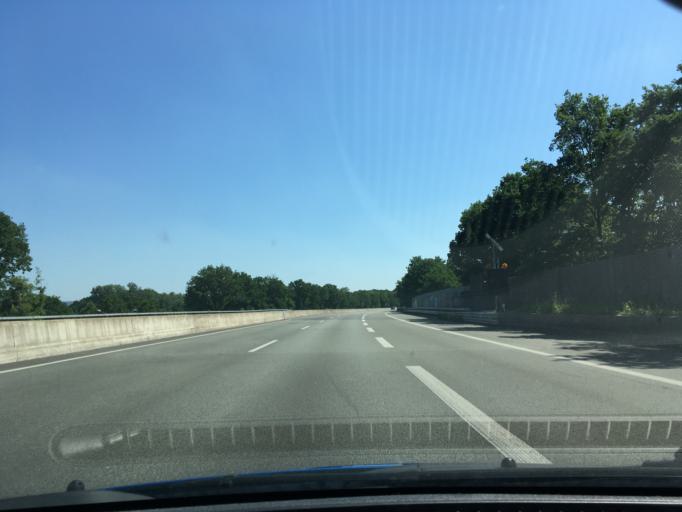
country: DE
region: North Rhine-Westphalia
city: Loehne
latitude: 52.2080
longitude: 8.7115
